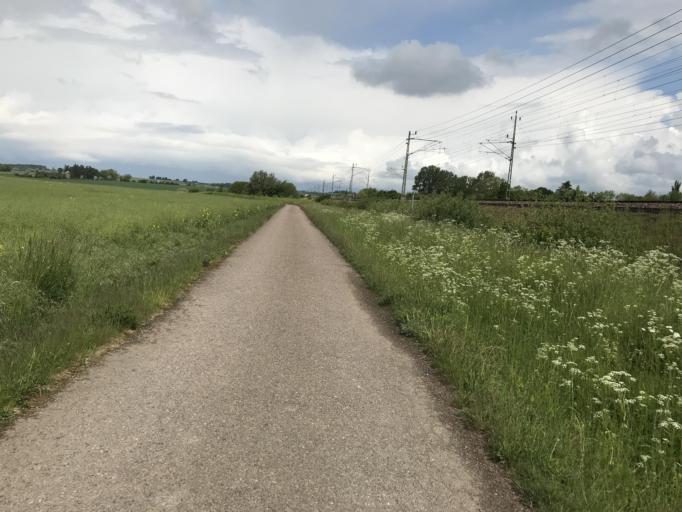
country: SE
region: Skane
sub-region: Landskrona
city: Landskrona
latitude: 55.9013
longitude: 12.8494
